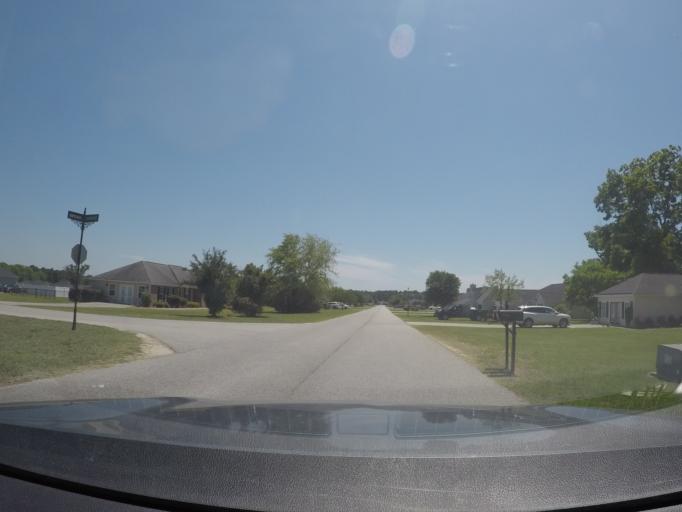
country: US
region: Georgia
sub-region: Bulloch County
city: Brooklet
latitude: 32.3554
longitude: -81.7558
